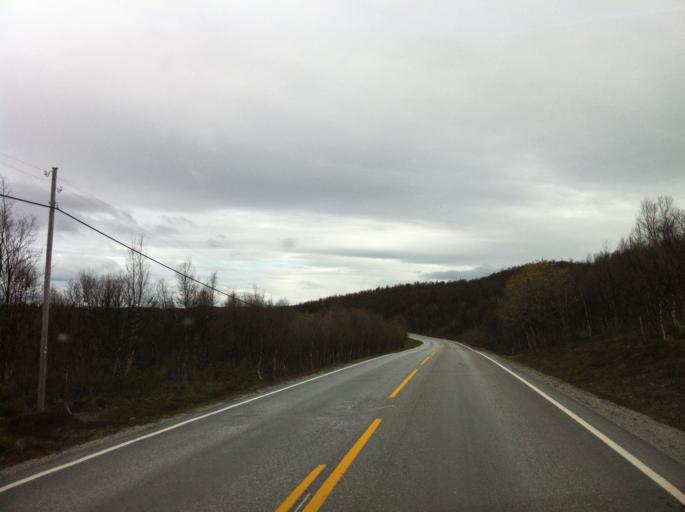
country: NO
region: Sor-Trondelag
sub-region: Tydal
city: Aas
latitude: 62.6353
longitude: 11.9579
